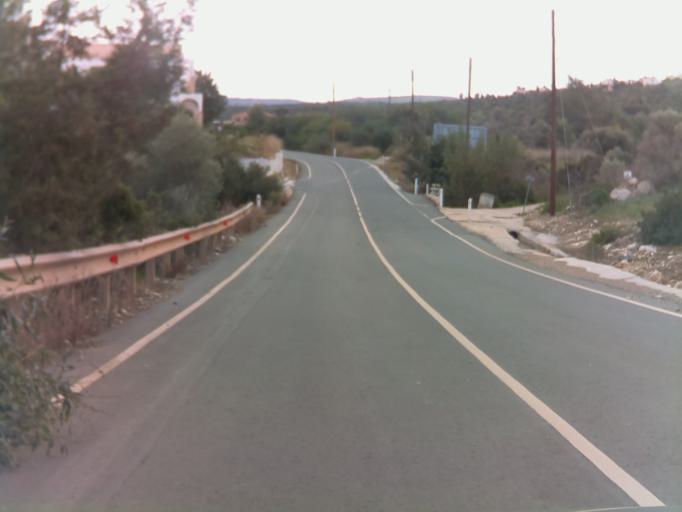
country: CY
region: Pafos
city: Polis
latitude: 35.0392
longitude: 32.3739
